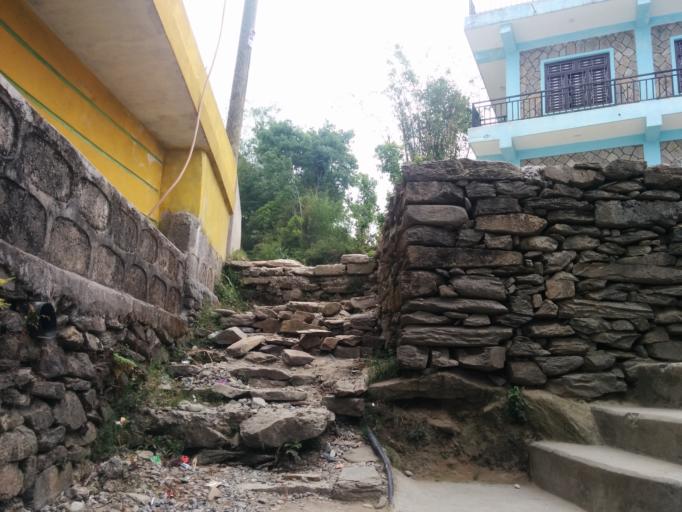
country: NP
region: Western Region
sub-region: Gandaki Zone
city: Pokhara
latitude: 28.2417
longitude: 83.9502
